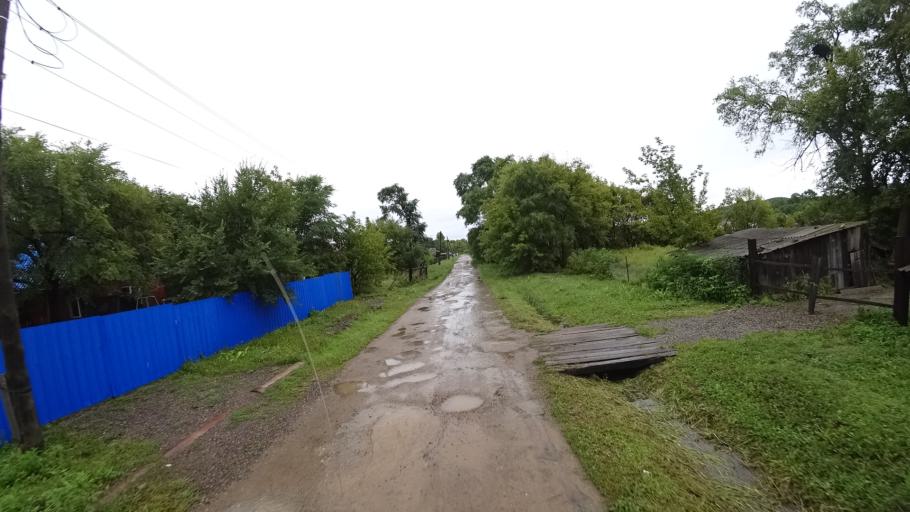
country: RU
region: Primorskiy
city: Monastyrishche
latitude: 44.2578
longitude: 132.4256
